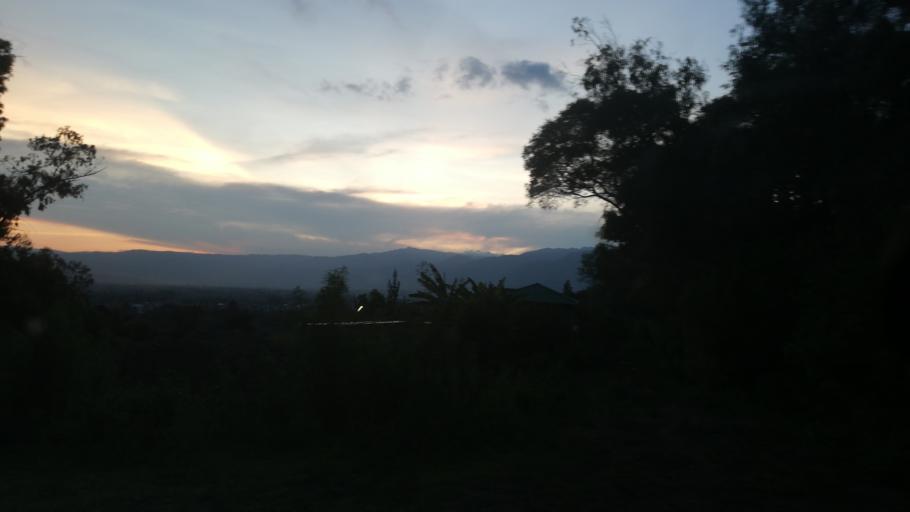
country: BO
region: Cochabamba
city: Cochabamba
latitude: -17.3290
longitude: -66.2082
